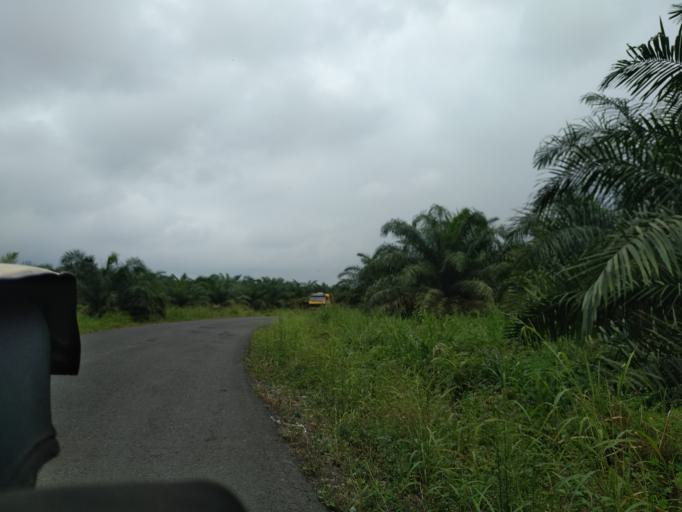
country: EC
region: Los Rios
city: Quevedo
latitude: -0.9678
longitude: -79.3513
